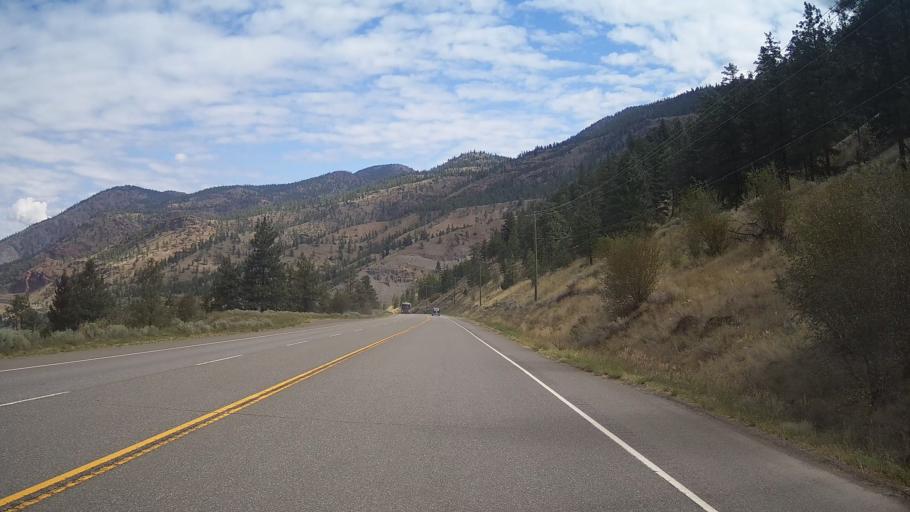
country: CA
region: British Columbia
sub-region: Thompson-Nicola Regional District
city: Ashcroft
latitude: 50.2889
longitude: -121.3983
